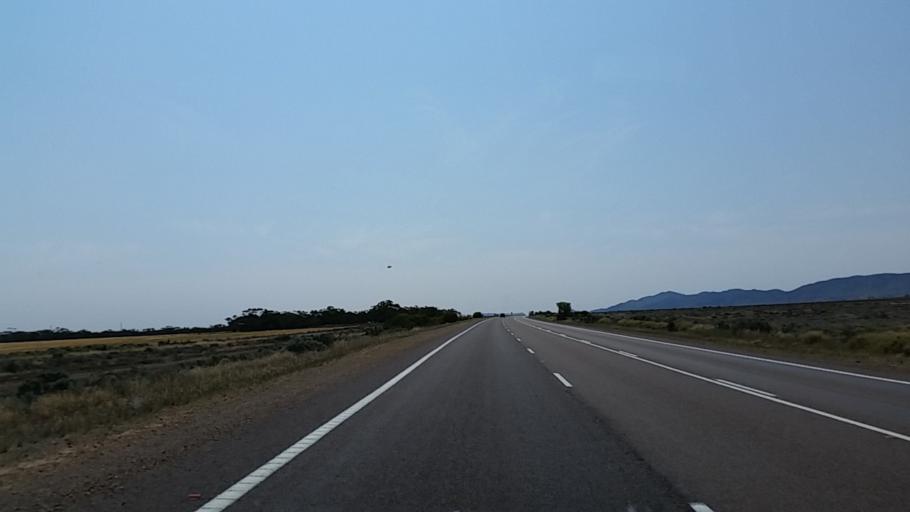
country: AU
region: South Australia
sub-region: Port Augusta
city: Port Augusta
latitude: -32.7201
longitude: 137.9398
